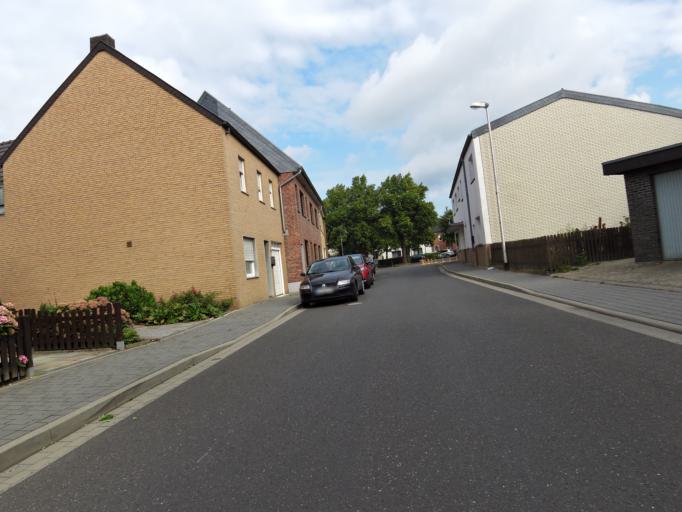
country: DE
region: North Rhine-Westphalia
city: Geilenkirchen
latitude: 50.9518
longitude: 6.0806
